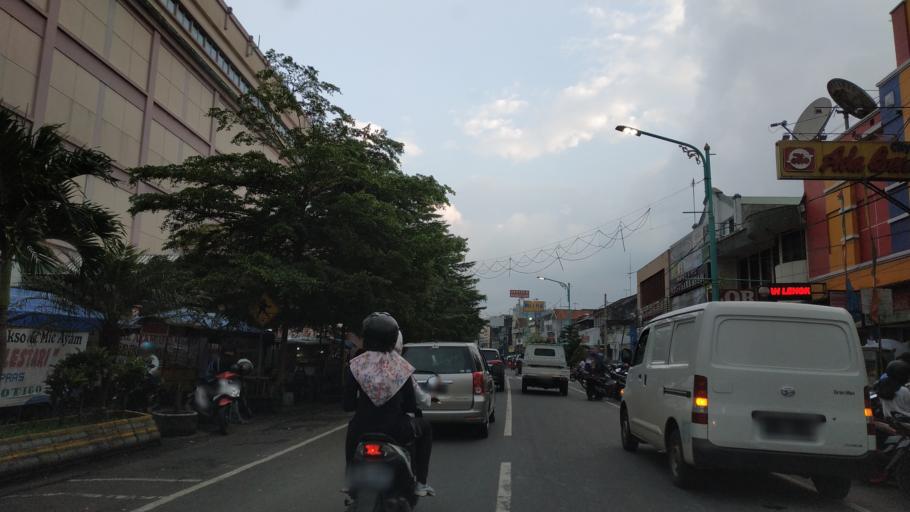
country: ID
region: Central Java
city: Salatiga
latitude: -7.3279
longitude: 110.5046
